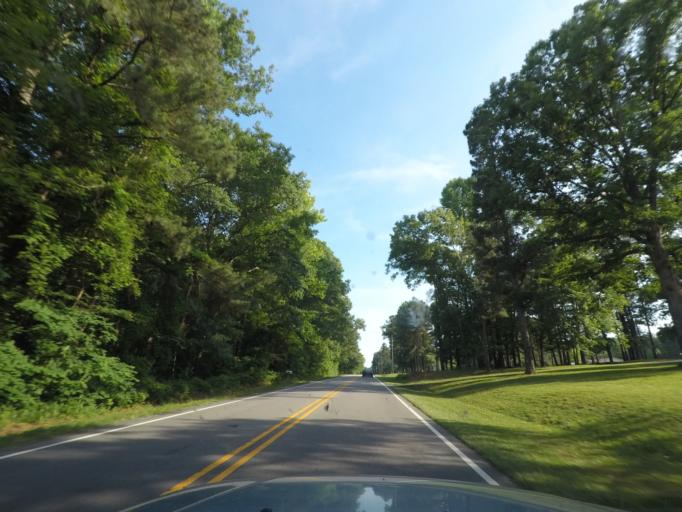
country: US
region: North Carolina
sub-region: Granville County
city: Oxford
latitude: 36.3881
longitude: -78.5932
